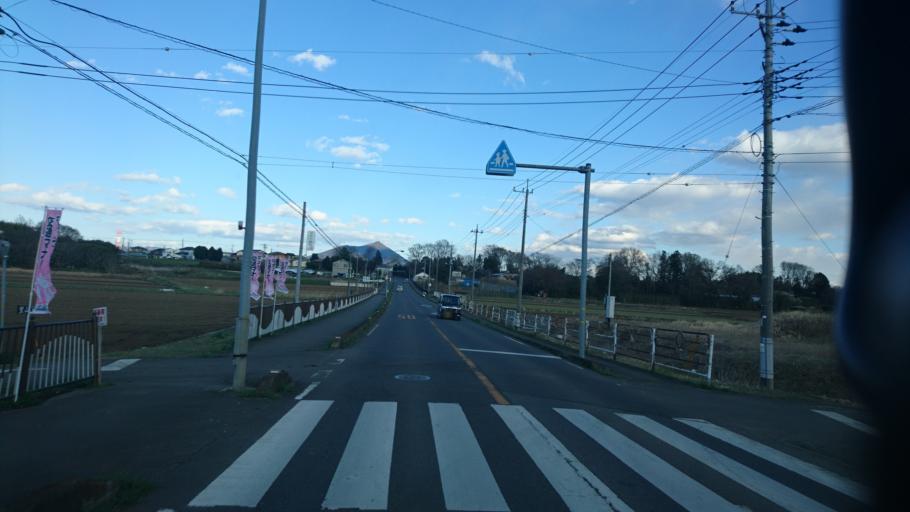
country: JP
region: Ibaraki
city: Shimodate
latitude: 36.2455
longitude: 139.9691
